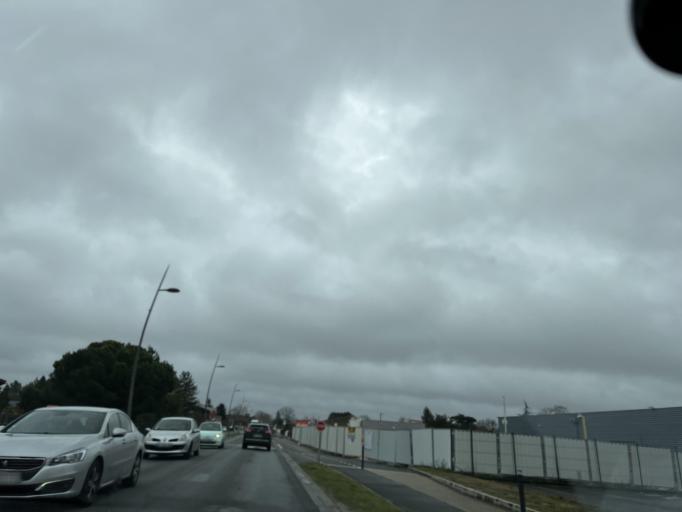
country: FR
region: Aquitaine
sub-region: Departement de la Gironde
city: Lesparre-Medoc
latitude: 45.3018
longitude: -0.9342
